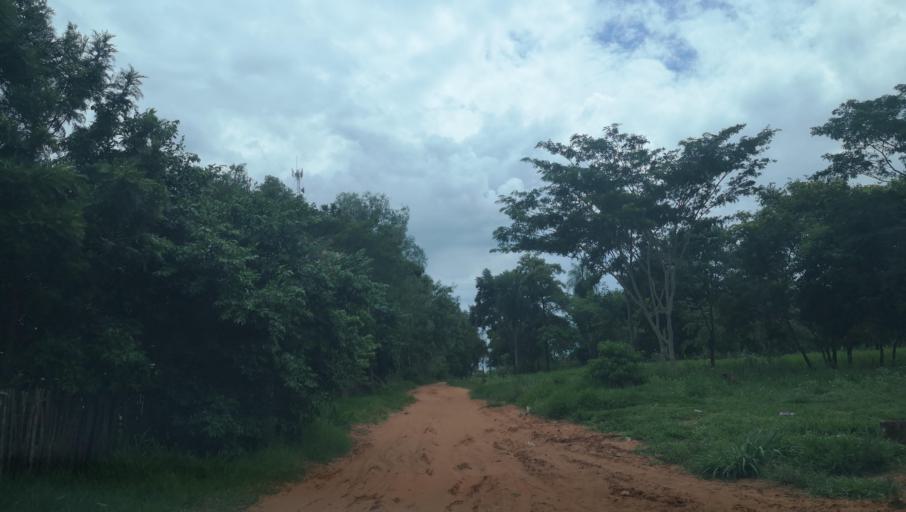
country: PY
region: San Pedro
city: Capiibary
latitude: -24.7240
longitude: -56.0105
